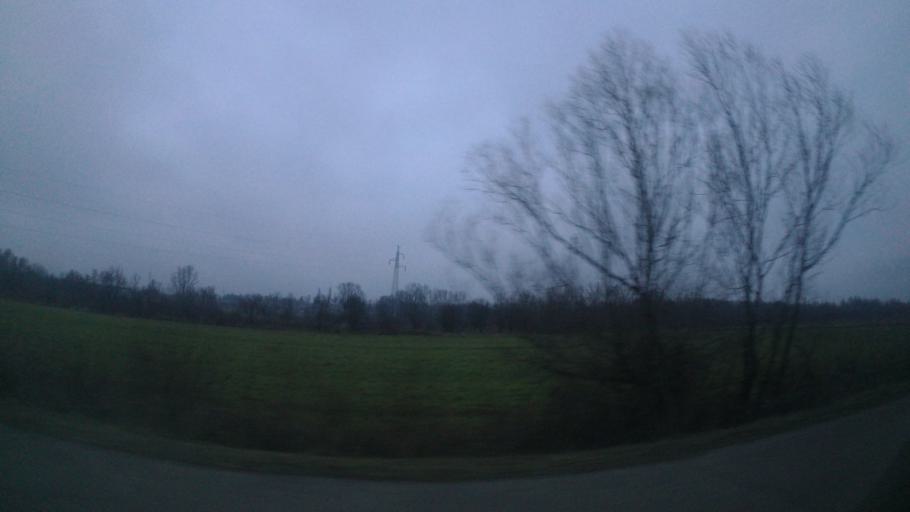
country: HR
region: Sisacko-Moslavacka
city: Petrinja
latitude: 45.4281
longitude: 16.3030
